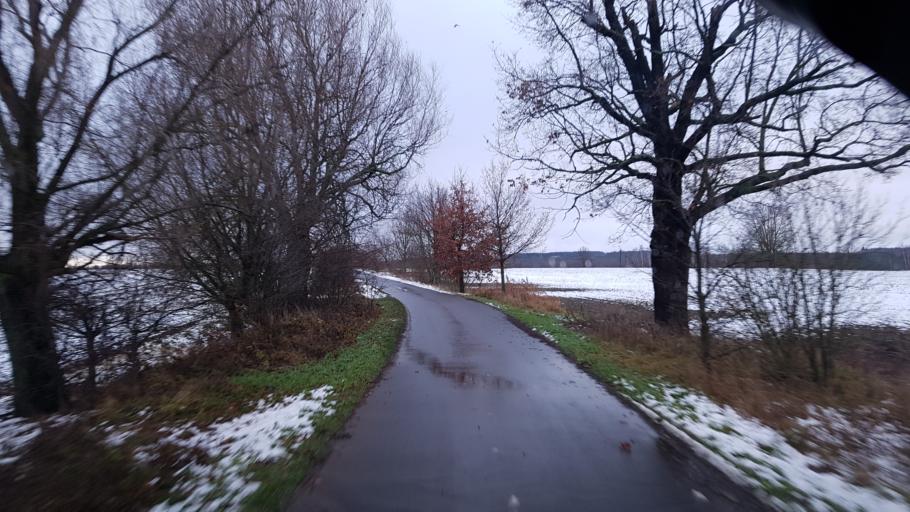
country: DE
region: Brandenburg
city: Crinitz
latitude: 51.7853
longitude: 13.7496
